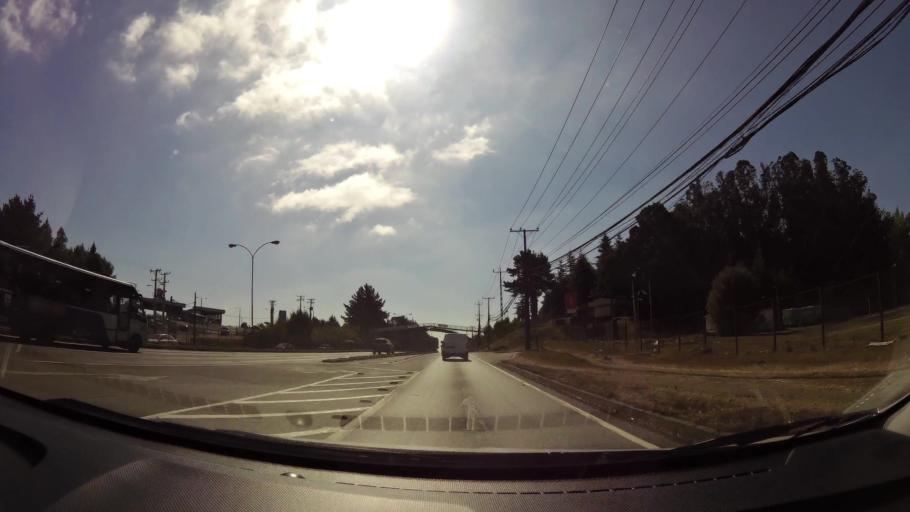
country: CL
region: Biobio
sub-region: Provincia de Concepcion
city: Concepcion
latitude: -36.7985
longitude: -73.0595
